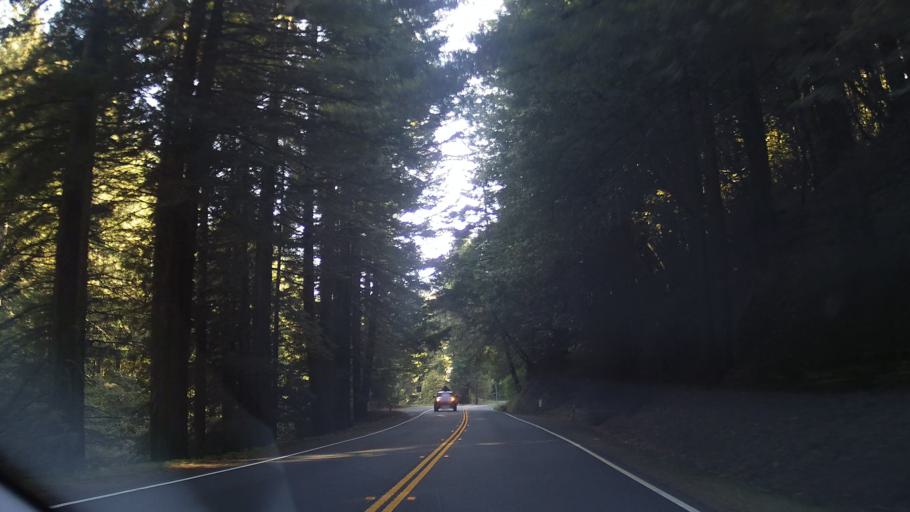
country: US
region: California
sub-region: Mendocino County
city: Brooktrails
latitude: 39.3481
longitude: -123.5905
